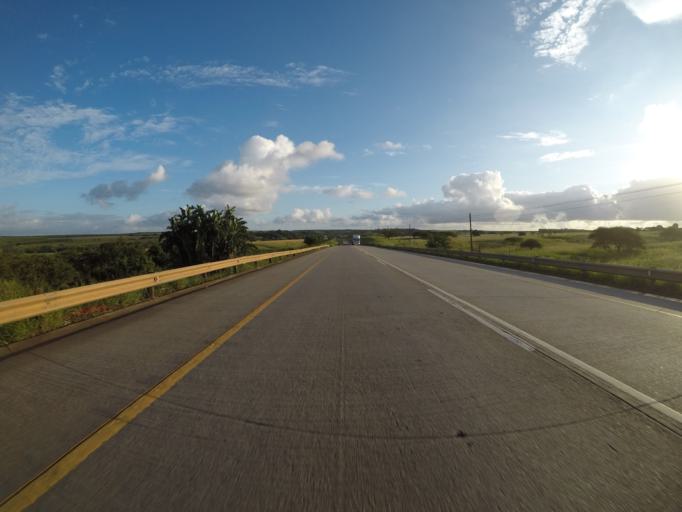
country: ZA
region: KwaZulu-Natal
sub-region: uMkhanyakude District Municipality
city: Mtubatuba
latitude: -28.4973
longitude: 32.1392
